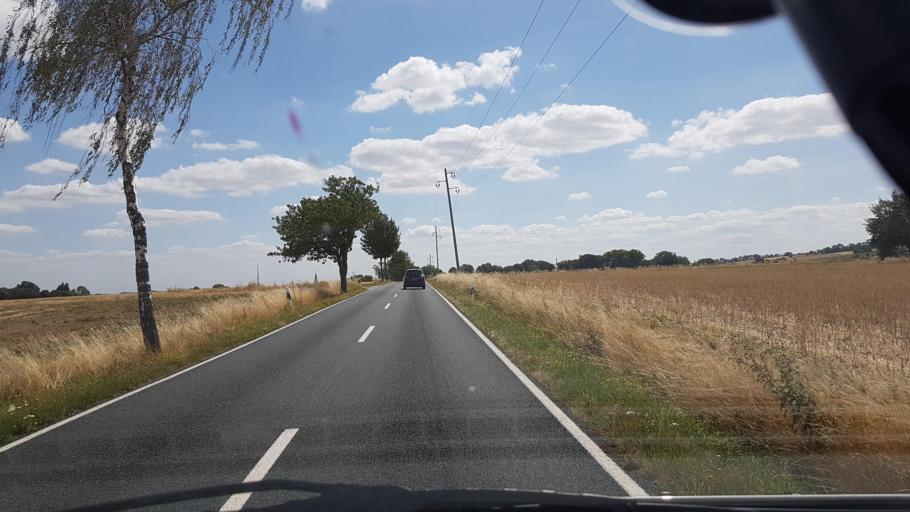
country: DE
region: Lower Saxony
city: Wolsdorf
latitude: 52.1666
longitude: 10.9561
